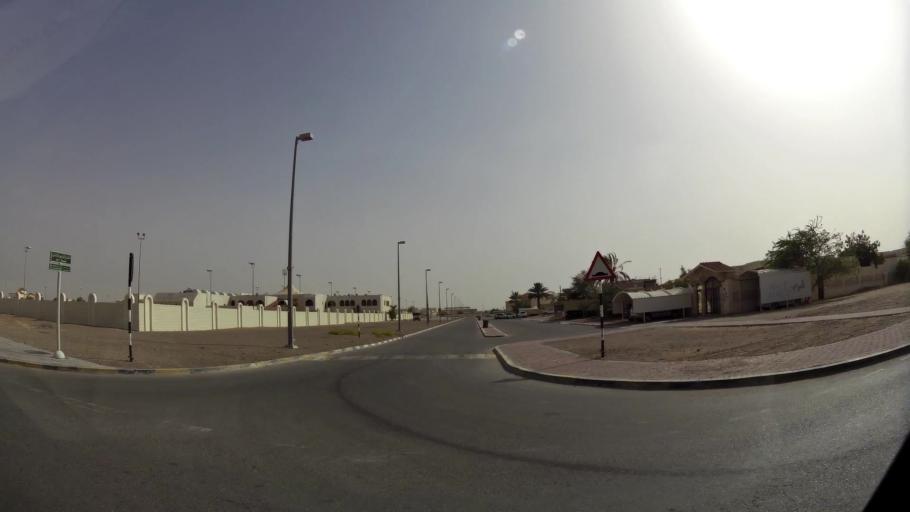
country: AE
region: Abu Dhabi
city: Al Ain
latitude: 24.2140
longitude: 55.5880
